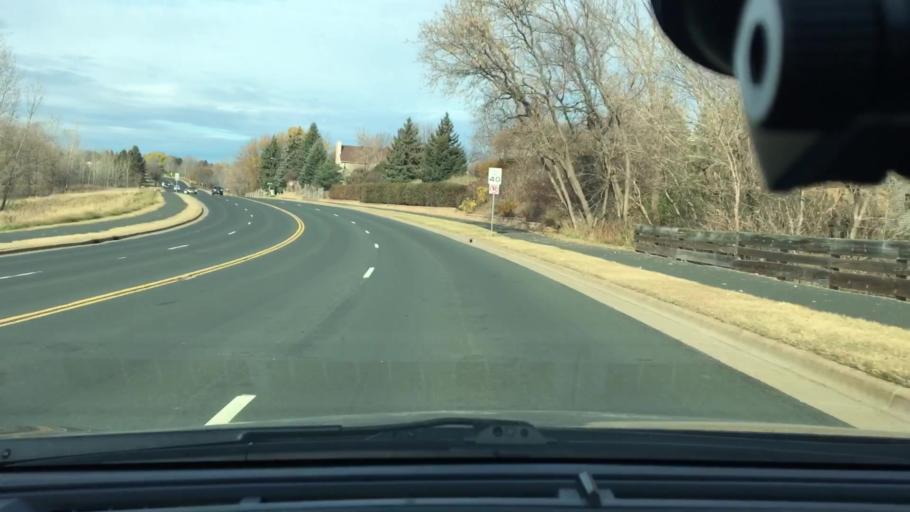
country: US
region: Minnesota
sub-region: Hennepin County
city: Maple Grove
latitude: 45.1062
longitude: -93.4788
